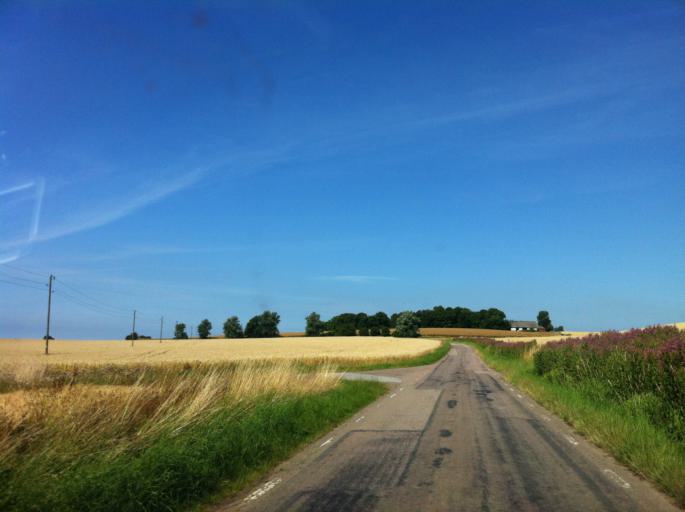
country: SE
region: Skane
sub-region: Landskrona
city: Asmundtorp
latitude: 55.8933
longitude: 12.9400
